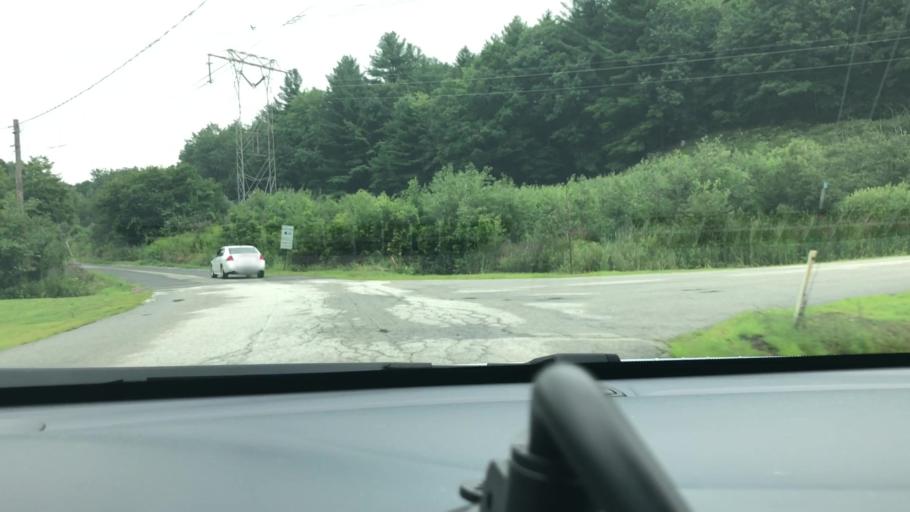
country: US
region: New Hampshire
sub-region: Hillsborough County
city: Pinardville
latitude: 42.9800
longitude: -71.5179
